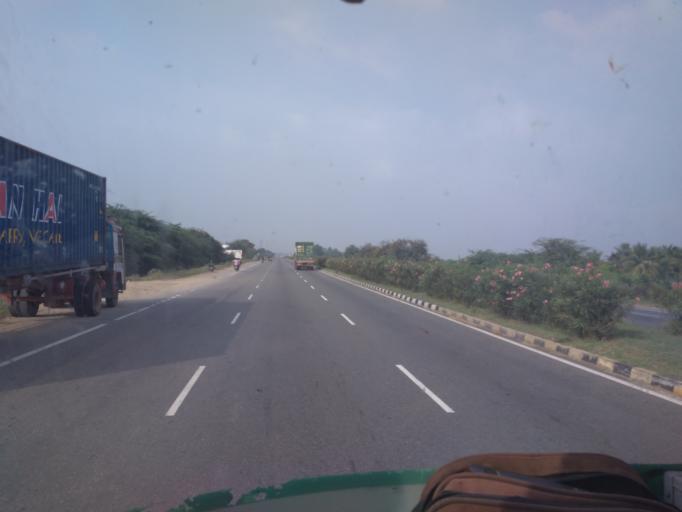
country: IN
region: Tamil Nadu
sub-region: Vellore
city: Vellore
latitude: 12.9168
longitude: 79.0411
